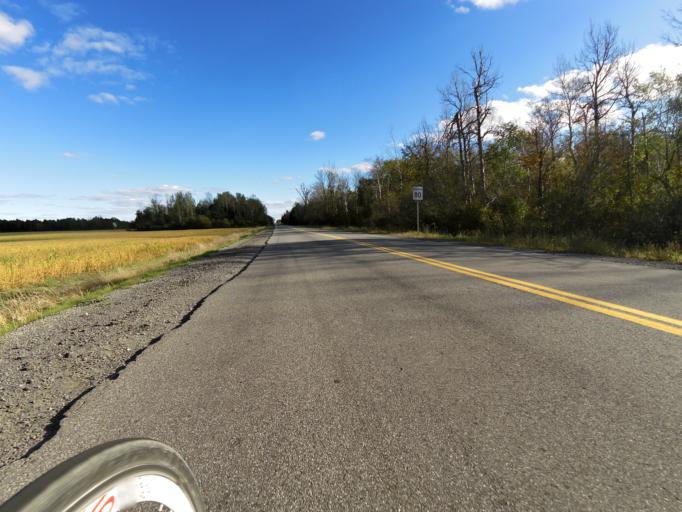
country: CA
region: Ontario
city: Bells Corners
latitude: 45.1510
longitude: -75.7739
